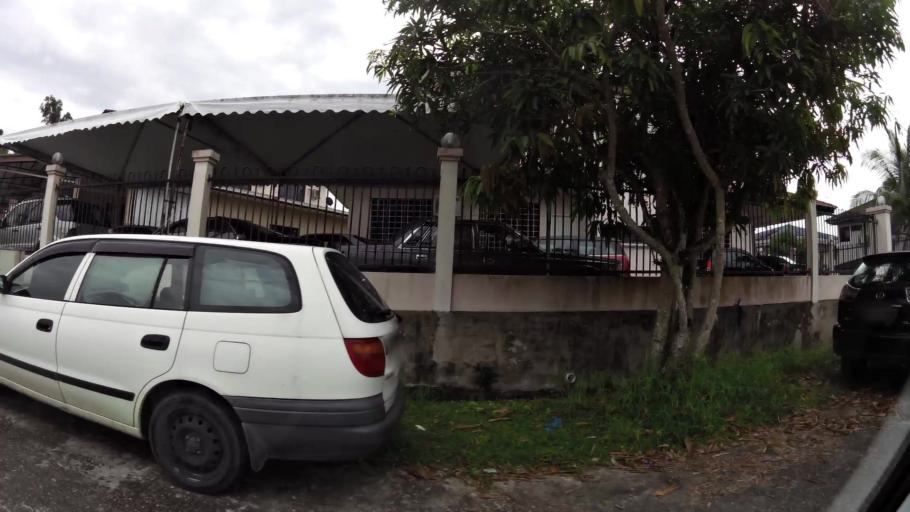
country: BN
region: Brunei and Muara
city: Bandar Seri Begawan
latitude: 4.8875
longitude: 114.9061
